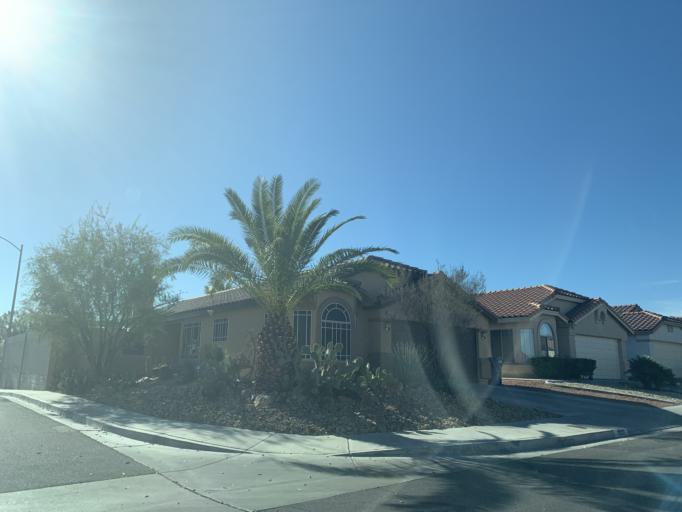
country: US
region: Nevada
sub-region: Clark County
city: Summerlin South
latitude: 36.1186
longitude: -115.2953
